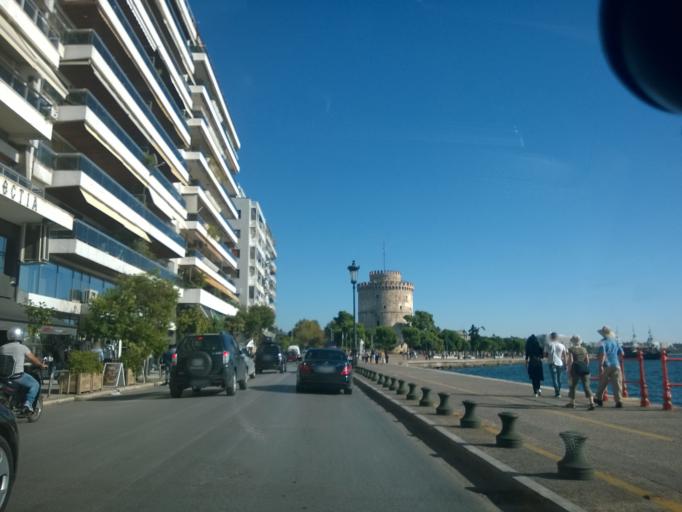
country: GR
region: Central Macedonia
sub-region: Nomos Thessalonikis
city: Agios Pavlos
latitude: 40.6280
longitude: 22.9466
